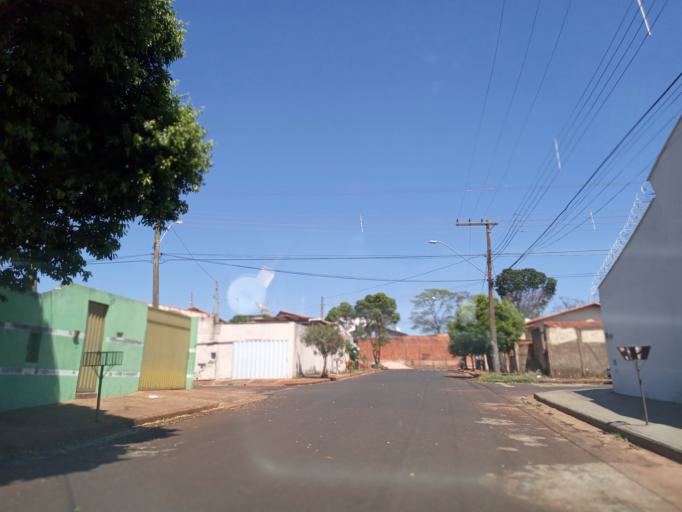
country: BR
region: Minas Gerais
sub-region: Ituiutaba
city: Ituiutaba
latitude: -18.9591
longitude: -49.4555
